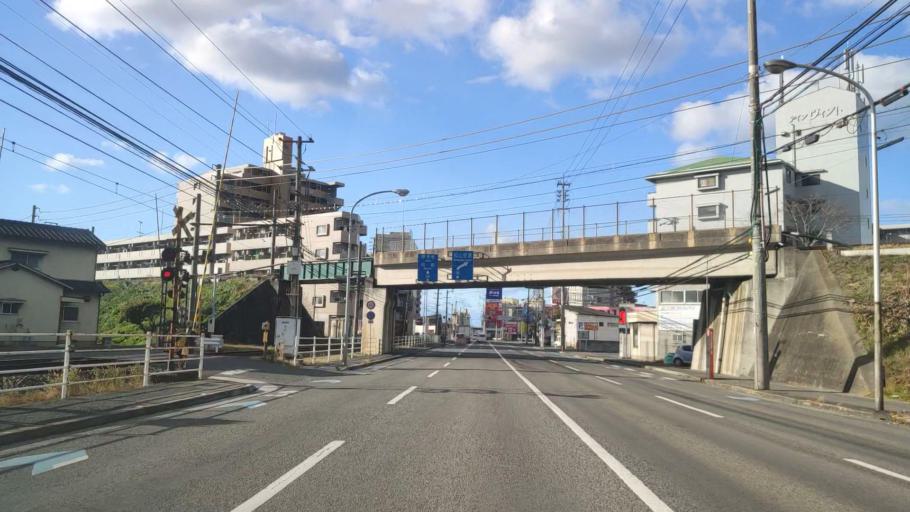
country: JP
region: Ehime
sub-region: Shikoku-chuo Shi
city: Matsuyama
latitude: 33.8298
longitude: 132.7519
